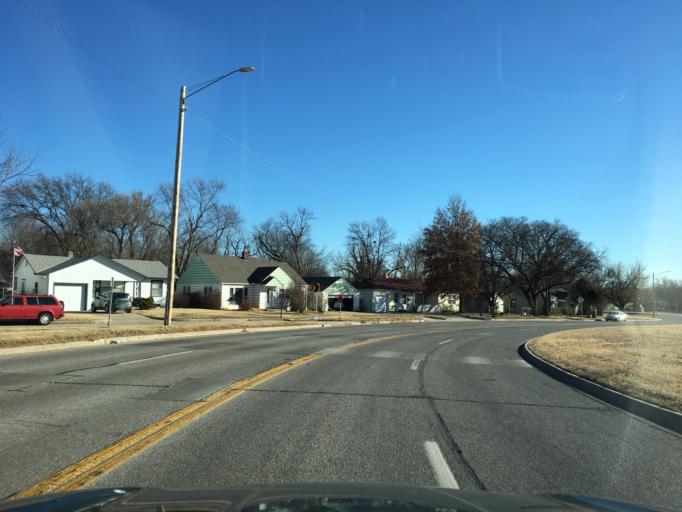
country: US
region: Kansas
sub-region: Sedgwick County
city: Wichita
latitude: 37.6735
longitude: -97.2902
